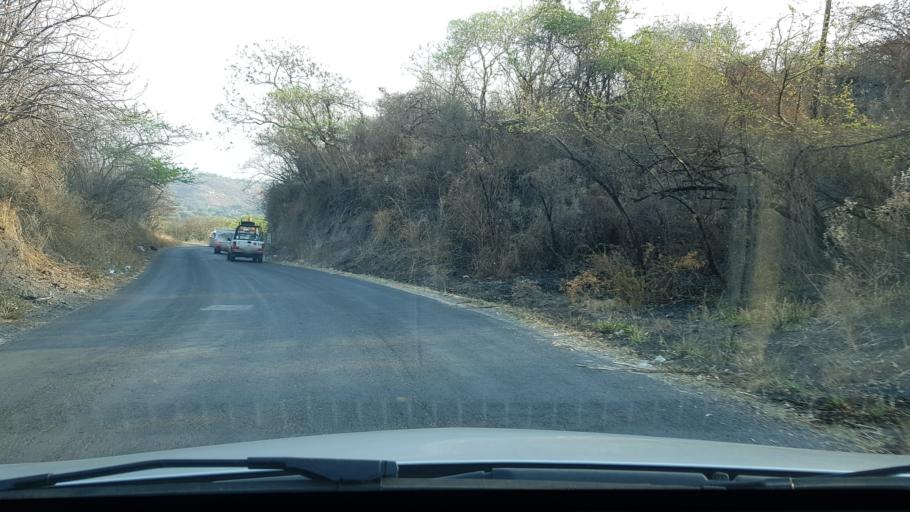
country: MX
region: Morelos
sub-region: Tepalcingo
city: Zacapalco
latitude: 18.6321
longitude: -99.0087
